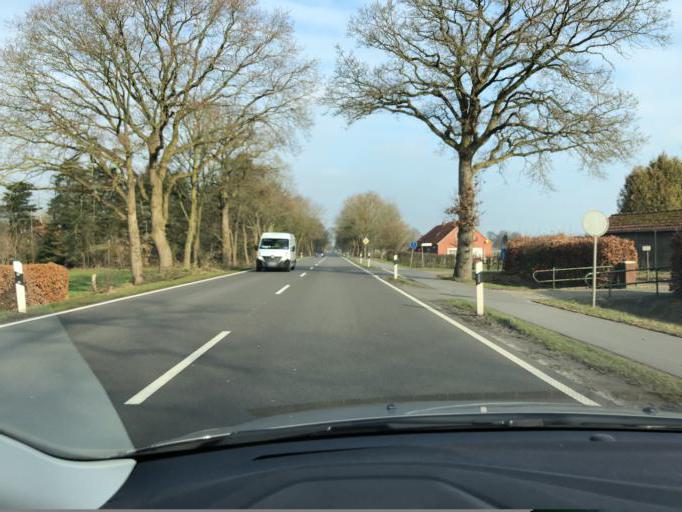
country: DE
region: Lower Saxony
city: Hesel
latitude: 53.3155
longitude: 7.5973
